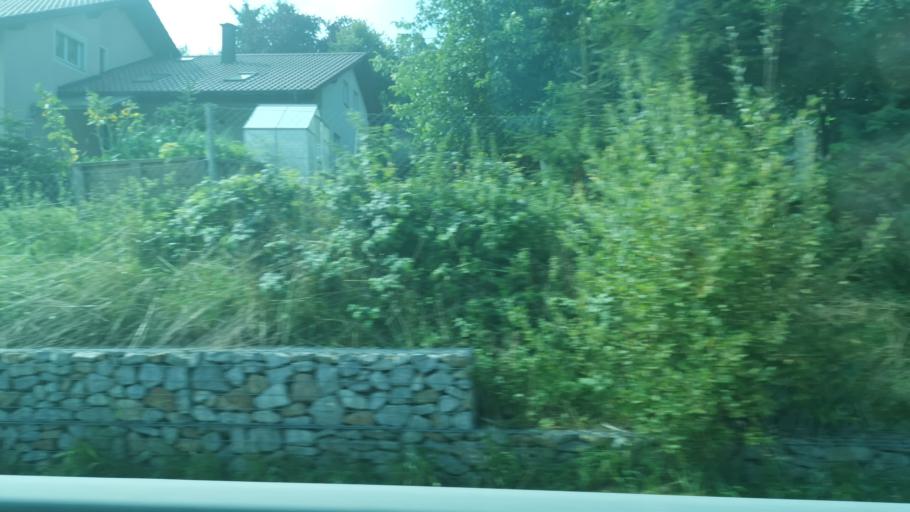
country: DE
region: Bavaria
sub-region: Upper Palatinate
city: Chamerau
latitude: 49.2068
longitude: 12.7297
